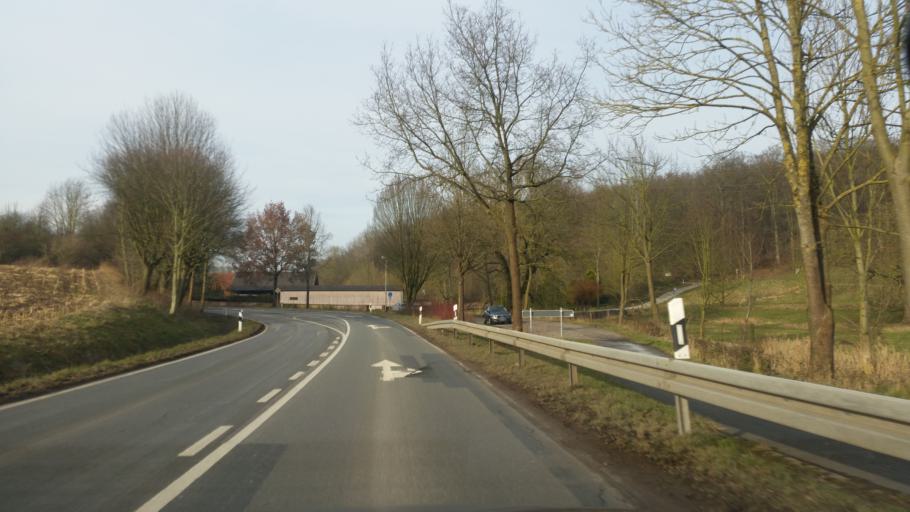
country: DE
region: Lower Saxony
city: Hameln
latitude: 52.1341
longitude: 9.3796
